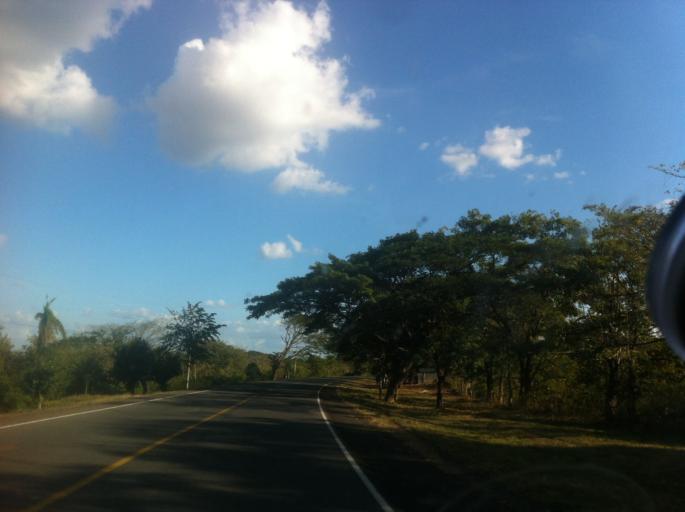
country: NI
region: Chontales
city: Acoyapa
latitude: 11.8314
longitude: -85.0373
